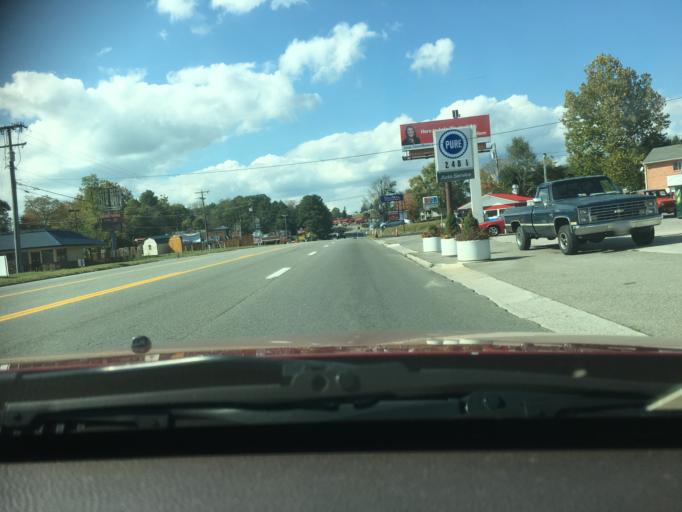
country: US
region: Virginia
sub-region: Pulaski County
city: Fairlawn
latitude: 37.1430
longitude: -80.5802
